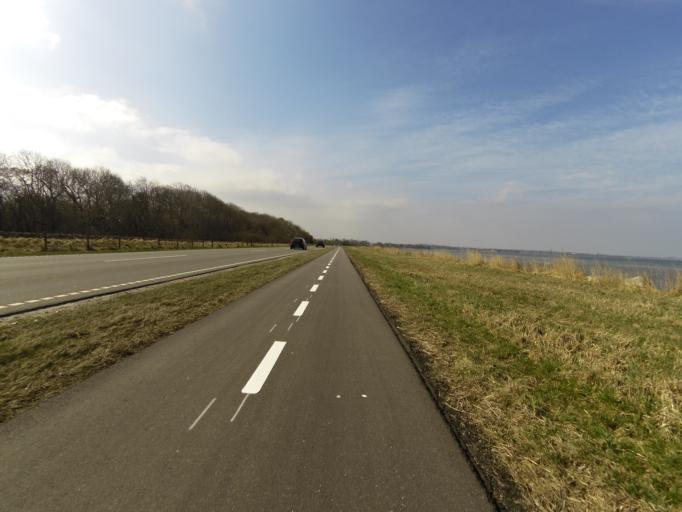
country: DK
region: Central Jutland
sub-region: Struer Kommune
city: Struer
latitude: 56.4666
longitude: 8.6528
